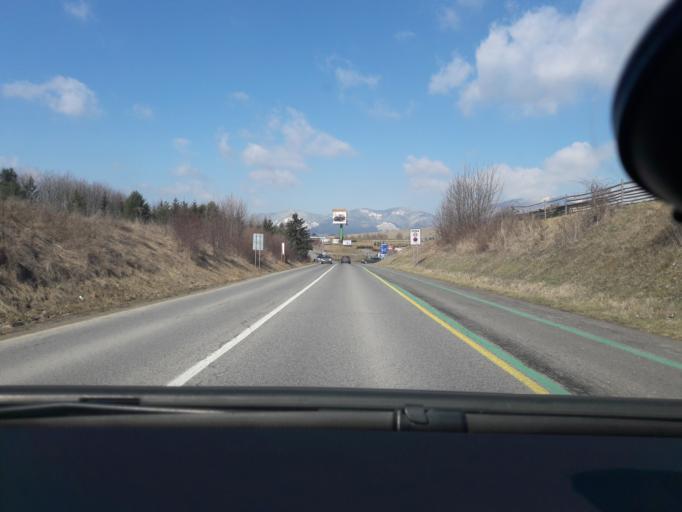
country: SK
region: Zilinsky
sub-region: Okres Liptovsky Mikulas
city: Liptovsky Mikulas
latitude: 49.1029
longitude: 19.5728
